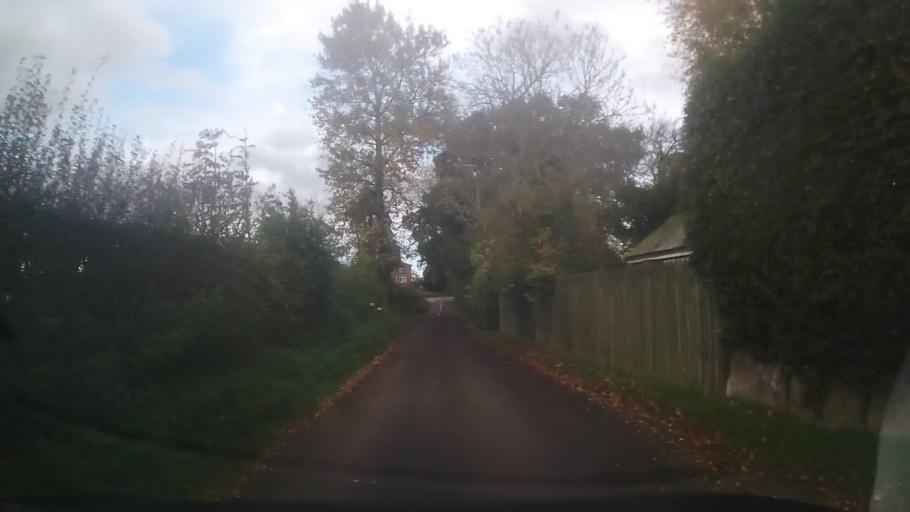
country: GB
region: England
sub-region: Shropshire
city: Wem
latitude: 52.8686
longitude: -2.7215
